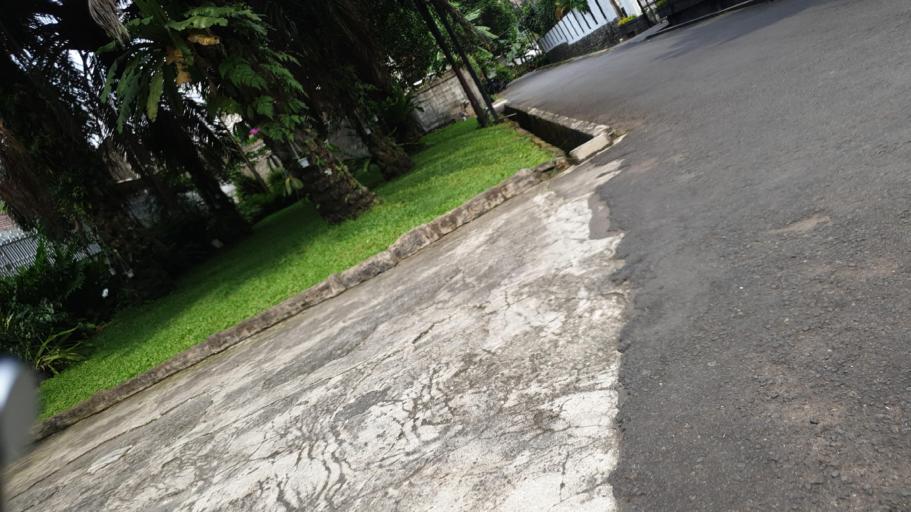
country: ID
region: Banten
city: South Tangerang
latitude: -6.2841
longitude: 106.7927
